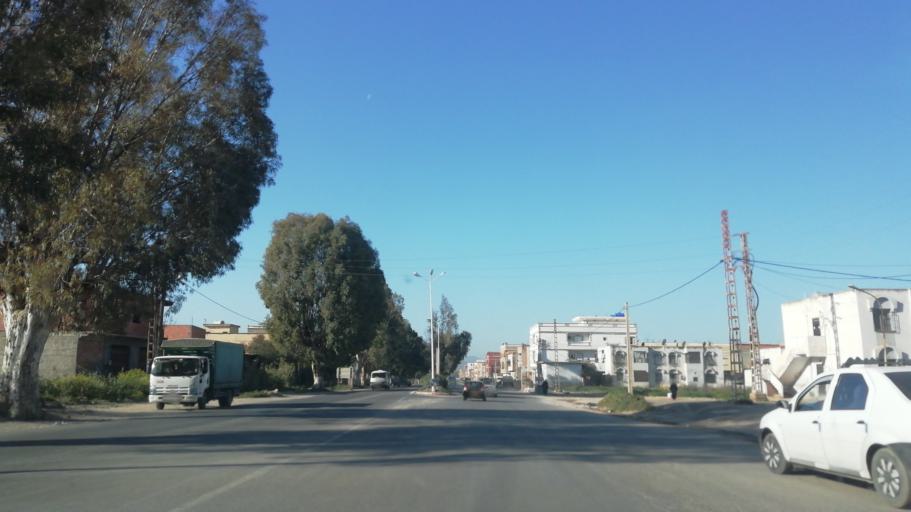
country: DZ
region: Mascara
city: Mascara
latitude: 35.6184
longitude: 0.1101
